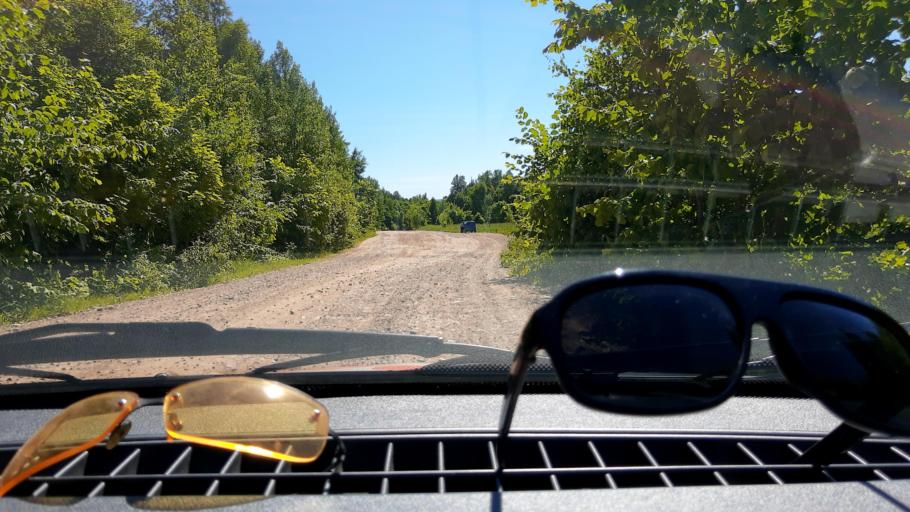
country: RU
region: Bashkortostan
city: Ulu-Telyak
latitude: 54.8040
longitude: 57.0341
